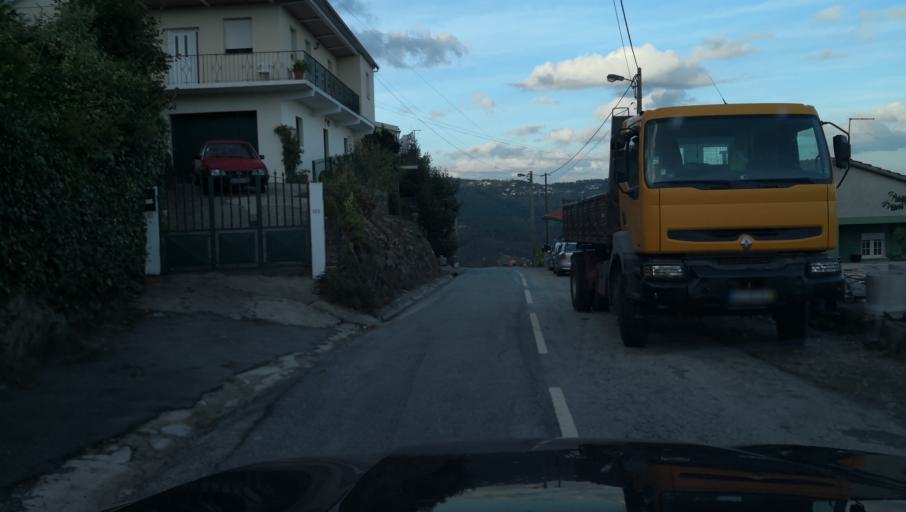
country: PT
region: Vila Real
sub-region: Santa Marta de Penaguiao
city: Santa Marta de Penaguiao
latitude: 41.2462
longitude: -7.8435
